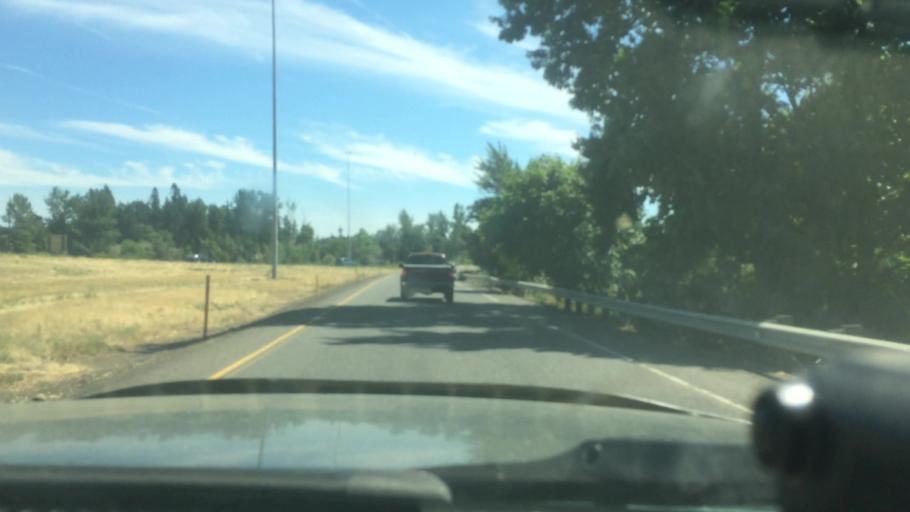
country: US
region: Oregon
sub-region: Lane County
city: Eugene
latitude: 44.0909
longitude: -123.1008
